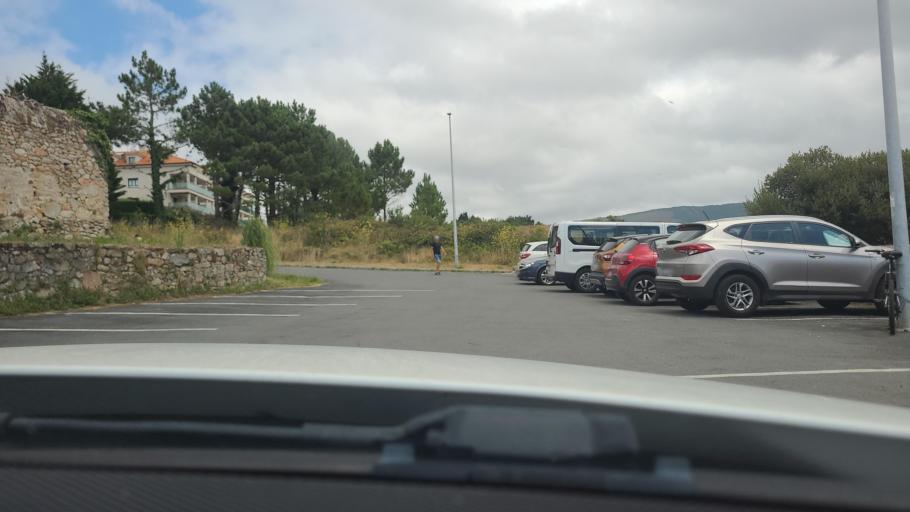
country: ES
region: Galicia
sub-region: Provincia da Coruna
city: Fisterra
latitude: 42.9152
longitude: -9.2664
